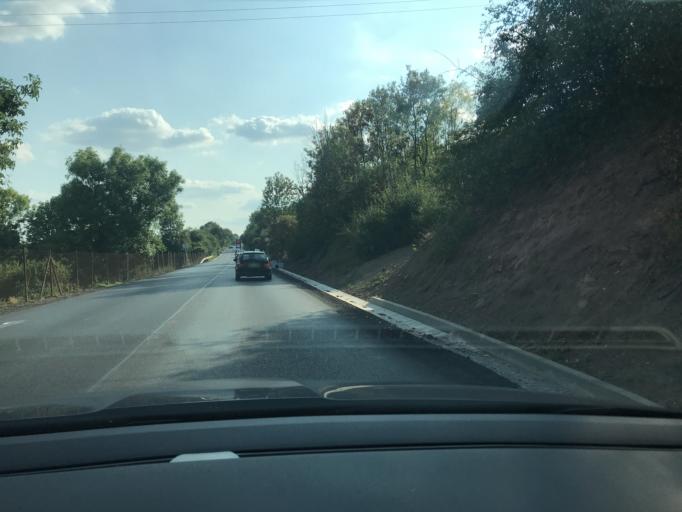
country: CZ
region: Central Bohemia
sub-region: Okres Kladno
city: Slany
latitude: 50.2456
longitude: 14.1397
